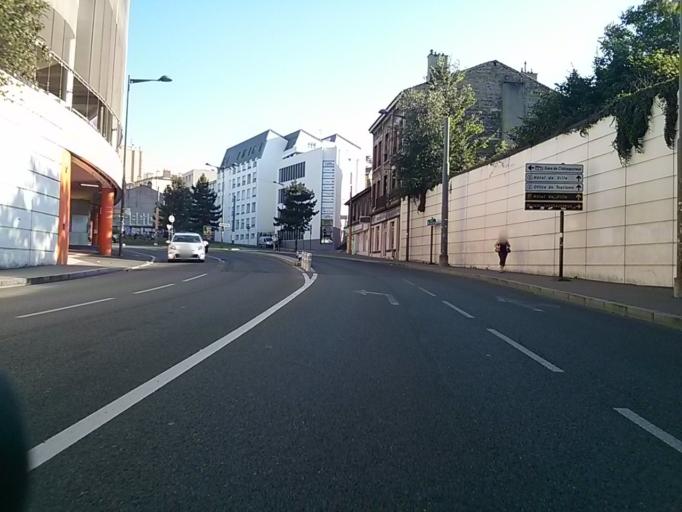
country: FR
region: Rhone-Alpes
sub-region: Departement de la Loire
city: Saint-Etienne
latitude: 45.4441
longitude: 4.3972
